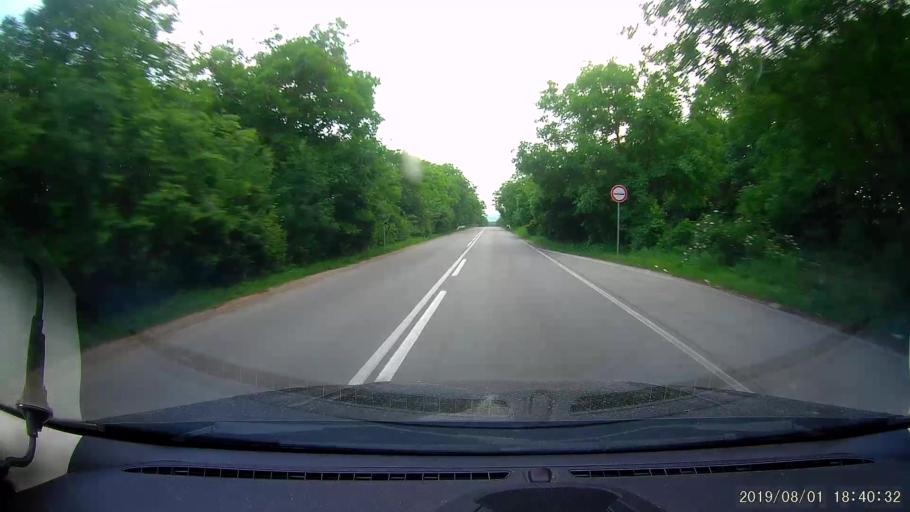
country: BG
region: Shumen
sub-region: Obshtina Khitrino
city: Gara Khitrino
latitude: 43.3651
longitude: 26.9196
